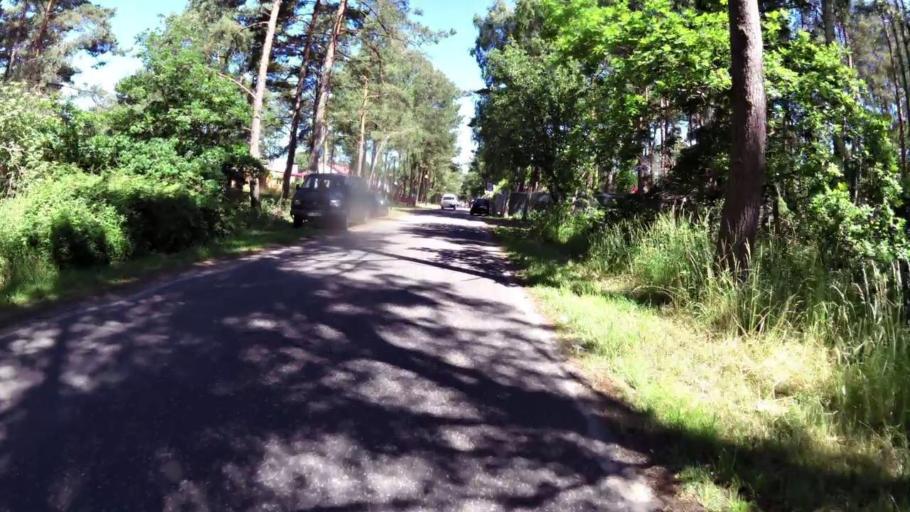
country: PL
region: West Pomeranian Voivodeship
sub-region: Powiat gryficki
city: Pobierowo
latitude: 54.0533
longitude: 14.9194
